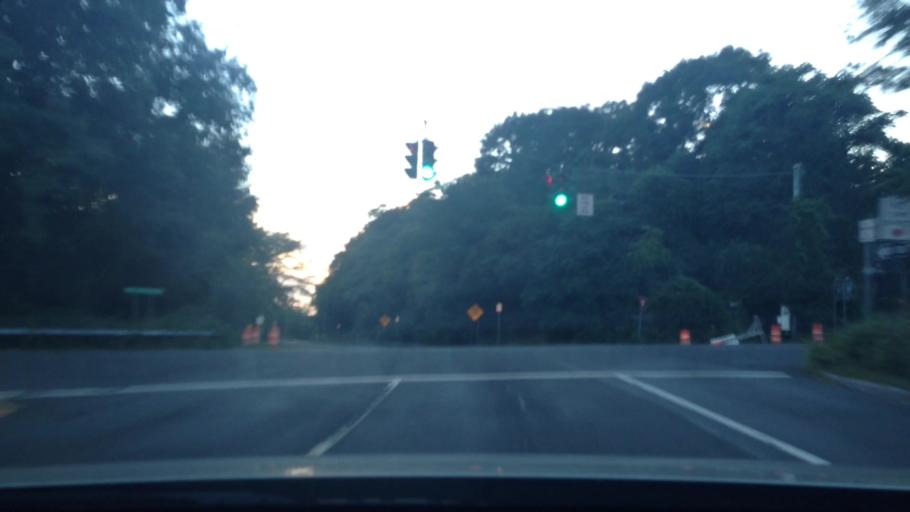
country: US
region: New York
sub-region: Suffolk County
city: Dix Hills
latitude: 40.7943
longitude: -73.3531
